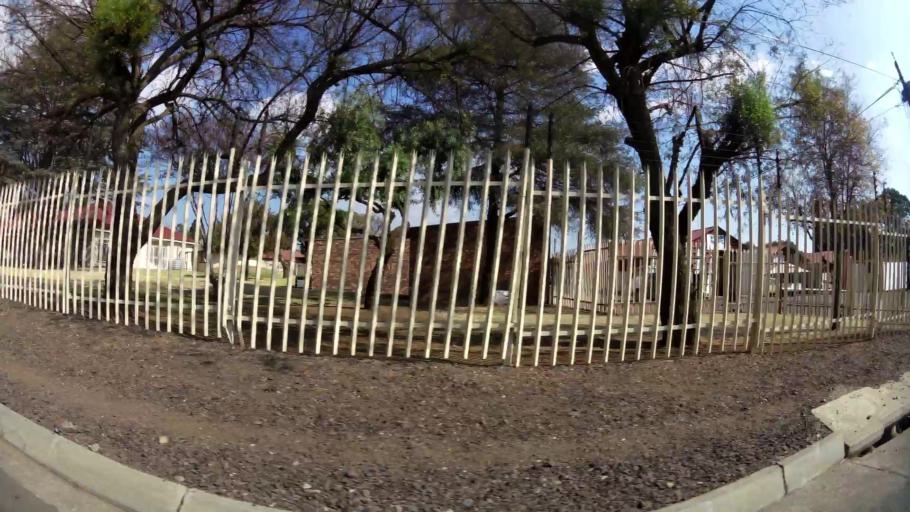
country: ZA
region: Gauteng
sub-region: City of Johannesburg Metropolitan Municipality
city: Modderfontein
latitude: -26.0890
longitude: 28.2538
